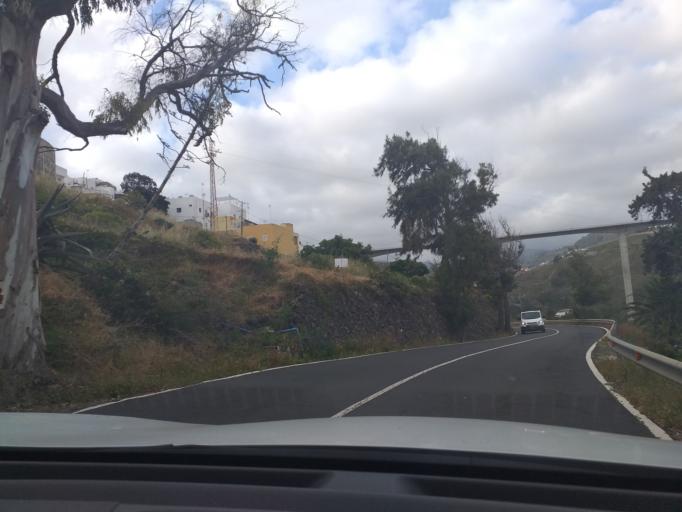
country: ES
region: Canary Islands
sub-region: Provincia de Las Palmas
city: Arucas
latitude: 28.1147
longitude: -15.4953
